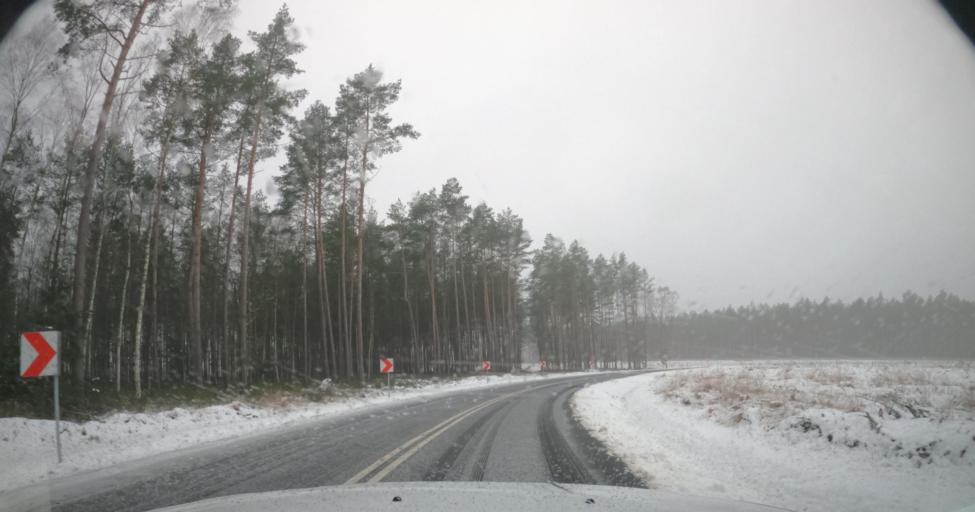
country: PL
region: West Pomeranian Voivodeship
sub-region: Powiat goleniowski
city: Goleniow
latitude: 53.6574
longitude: 14.8175
